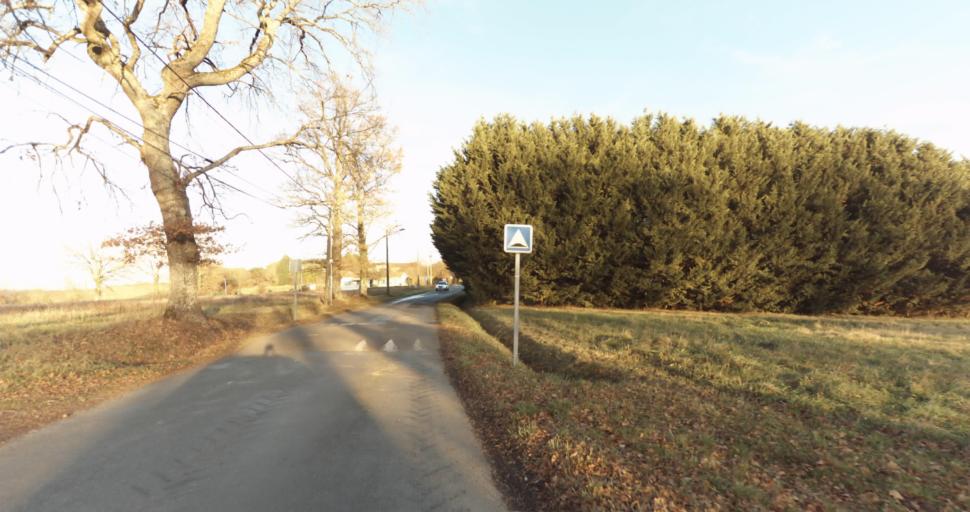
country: FR
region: Limousin
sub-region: Departement de la Haute-Vienne
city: Aixe-sur-Vienne
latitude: 45.8154
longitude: 1.1411
